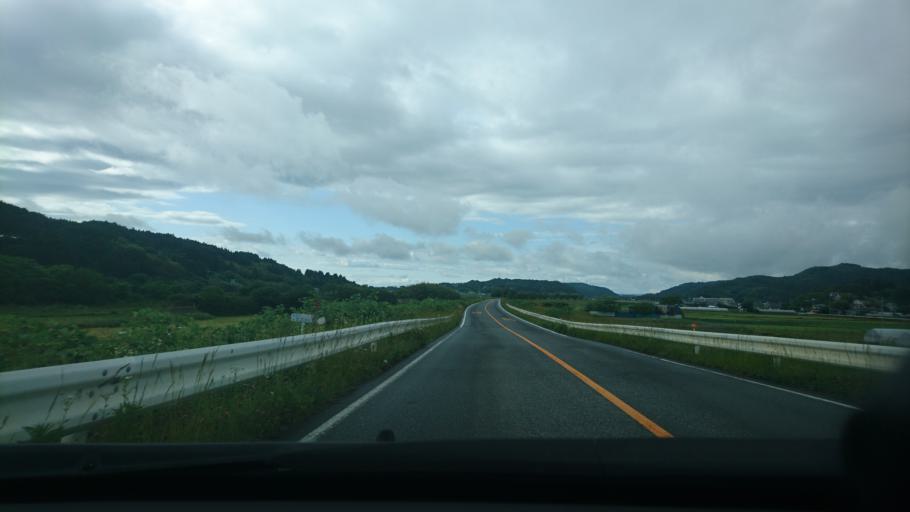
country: JP
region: Miyagi
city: Wakuya
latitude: 38.6404
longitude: 141.2880
